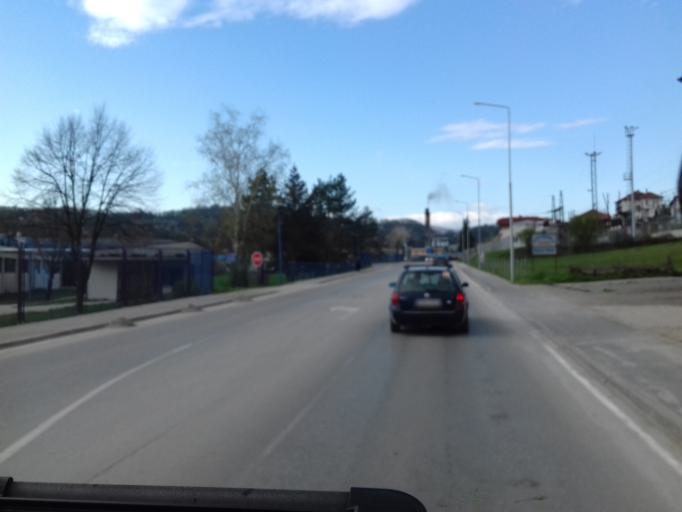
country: BA
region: Federation of Bosnia and Herzegovina
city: Tesanj
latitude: 44.6265
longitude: 17.9998
